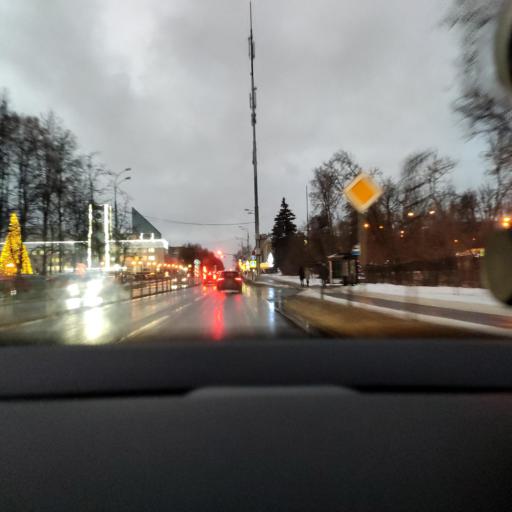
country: RU
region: Moskovskaya
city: Mytishchi
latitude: 55.9093
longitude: 37.7387
